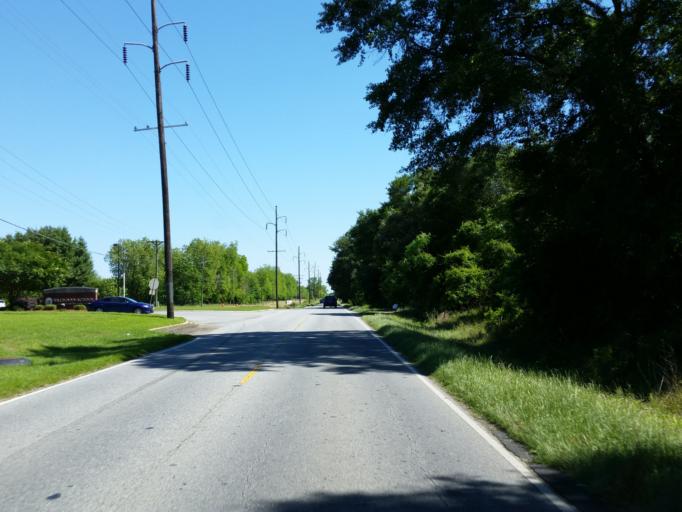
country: US
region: Georgia
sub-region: Lowndes County
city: Hahira
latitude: 30.9214
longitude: -83.3492
